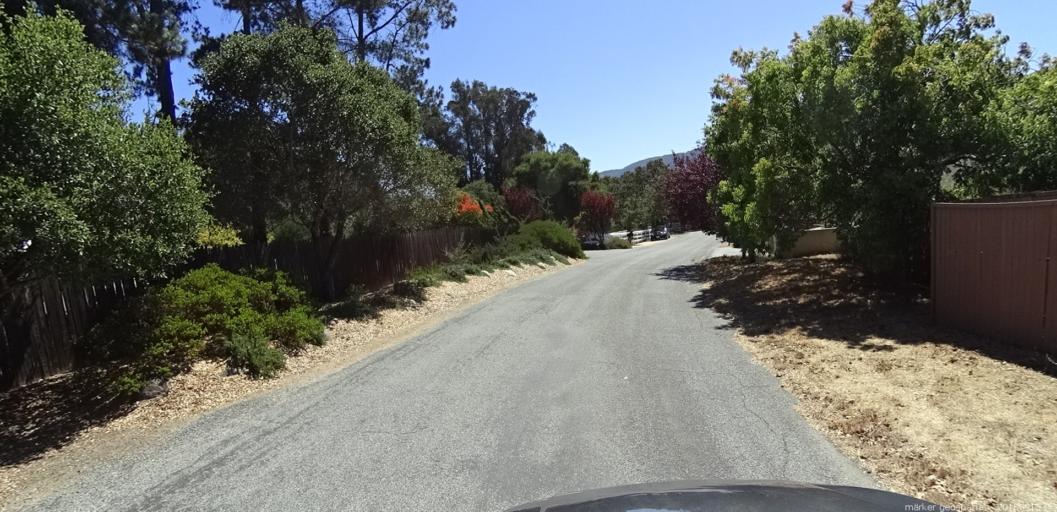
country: US
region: California
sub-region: Monterey County
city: Carmel Valley Village
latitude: 36.5048
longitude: -121.7548
